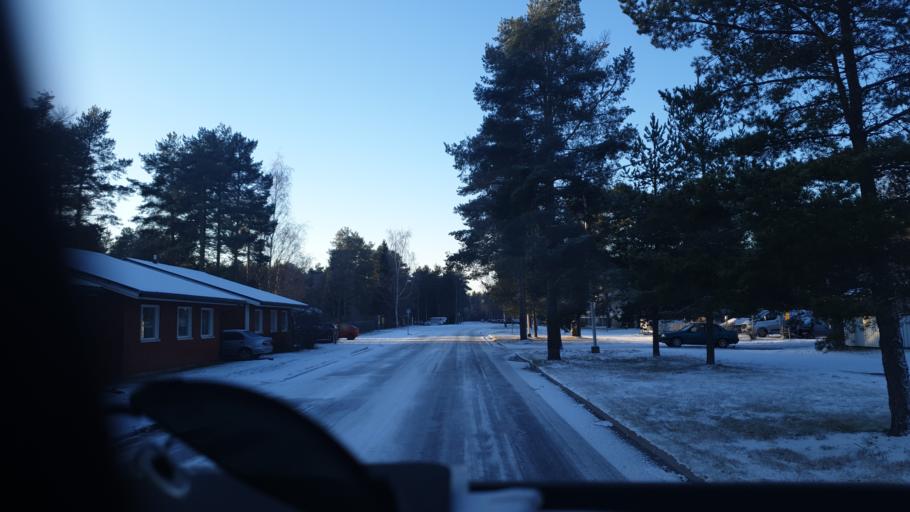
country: FI
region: Central Ostrobothnia
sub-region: Kokkola
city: Kokkola
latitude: 63.8234
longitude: 23.0774
